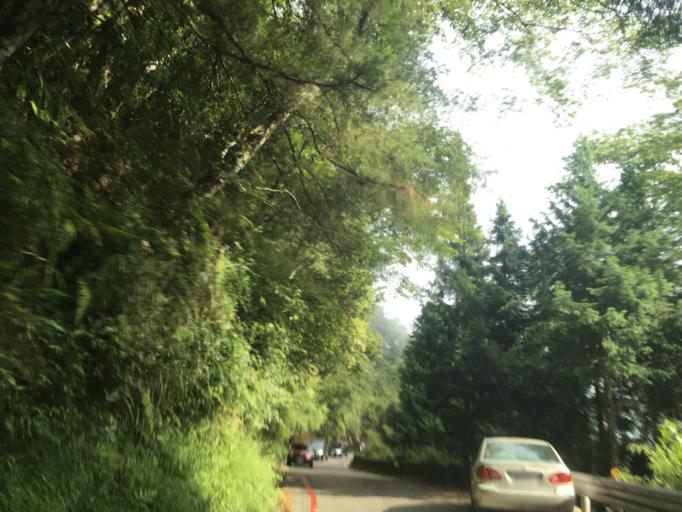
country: TW
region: Taiwan
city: Fengyuan
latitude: 24.2344
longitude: 120.9586
